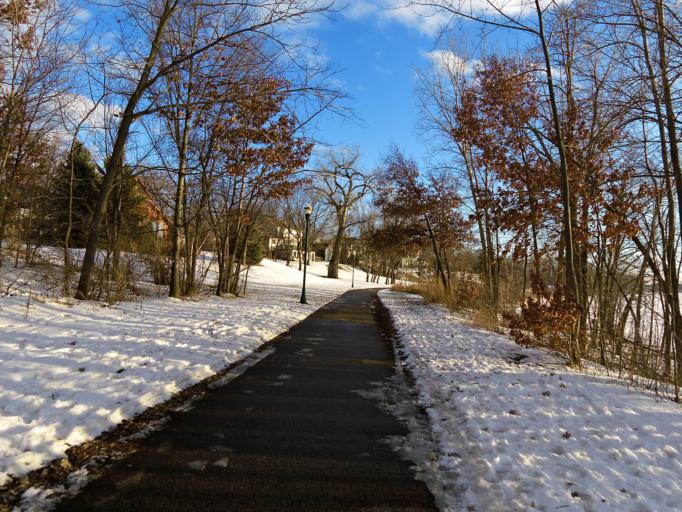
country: US
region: Wisconsin
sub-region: Saint Croix County
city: Hudson
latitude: 44.9818
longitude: -92.7602
